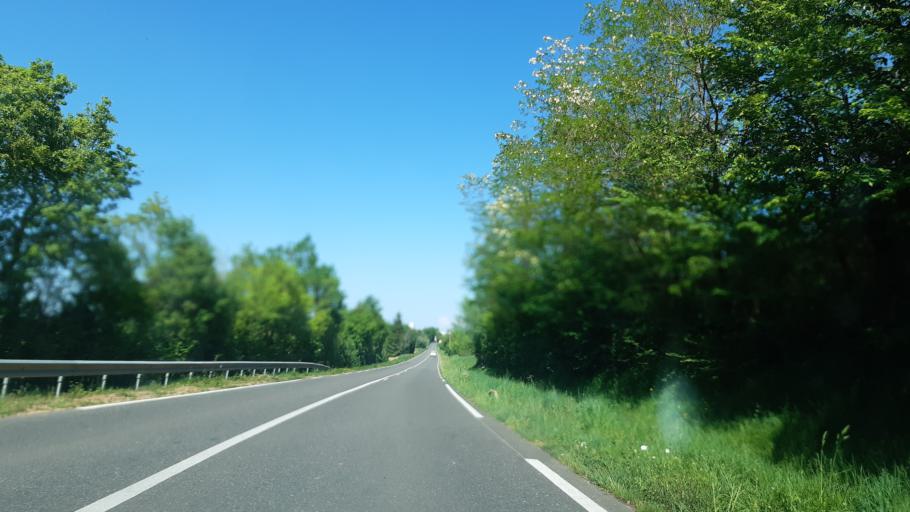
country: FR
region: Midi-Pyrenees
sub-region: Departement du Gers
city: Pujaudran
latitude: 43.5909
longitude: 1.0551
